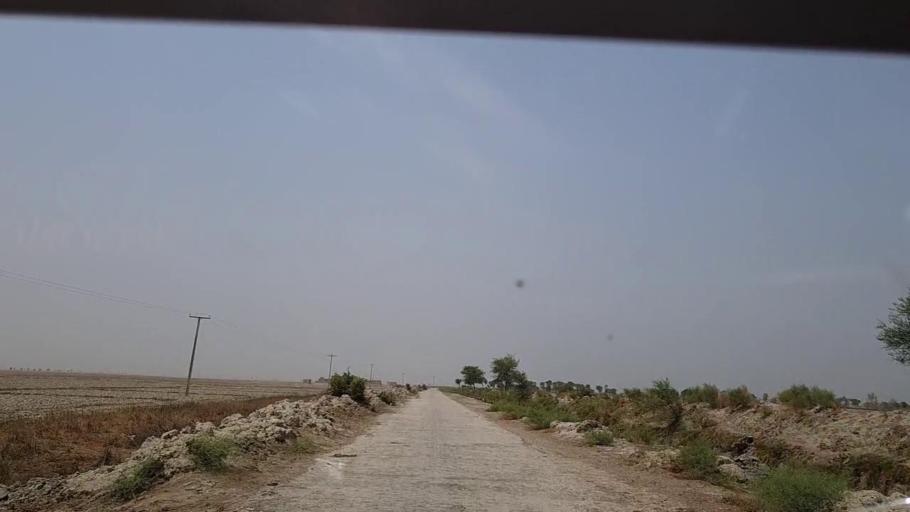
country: PK
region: Sindh
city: Khairpur Nathan Shah
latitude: 27.0360
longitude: 67.6191
